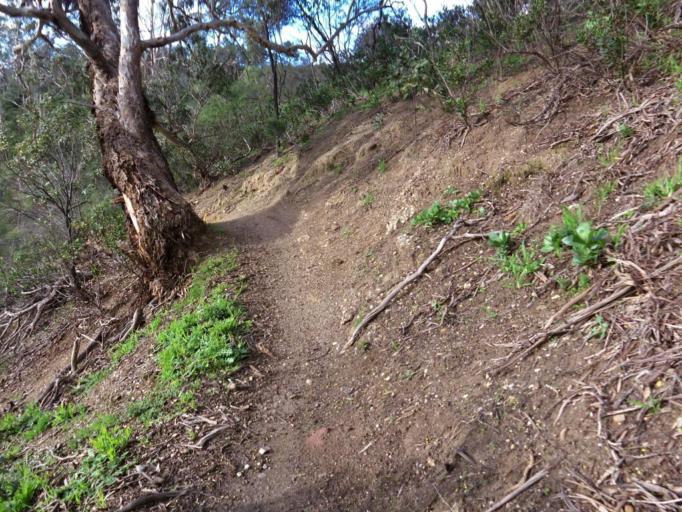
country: AU
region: Victoria
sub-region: Whittlesea
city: Mill Park
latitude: -37.6749
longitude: 145.0892
